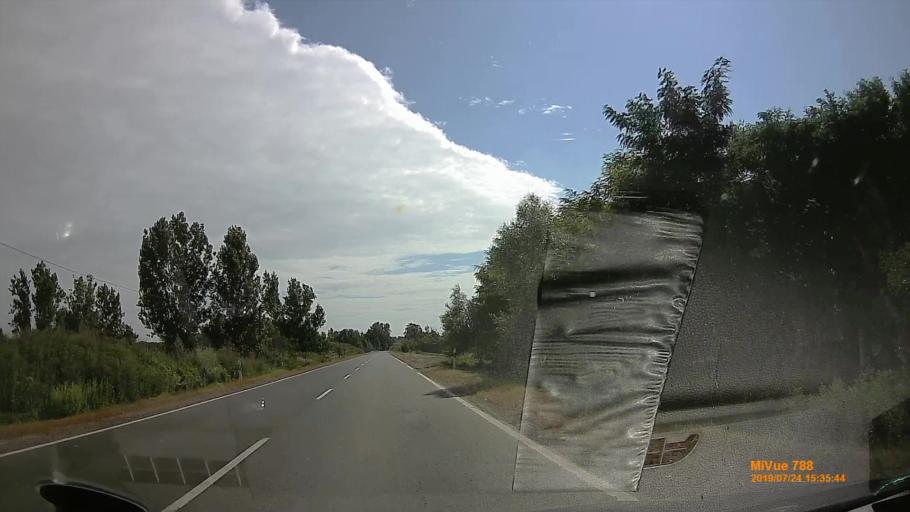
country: HU
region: Szabolcs-Szatmar-Bereg
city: Vasarosnameny
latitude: 48.1325
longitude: 22.3524
